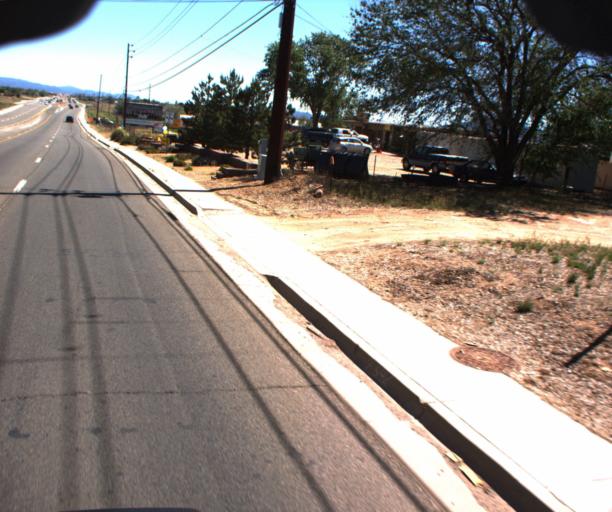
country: US
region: Arizona
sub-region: Yavapai County
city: Chino Valley
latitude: 34.7440
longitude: -112.4547
